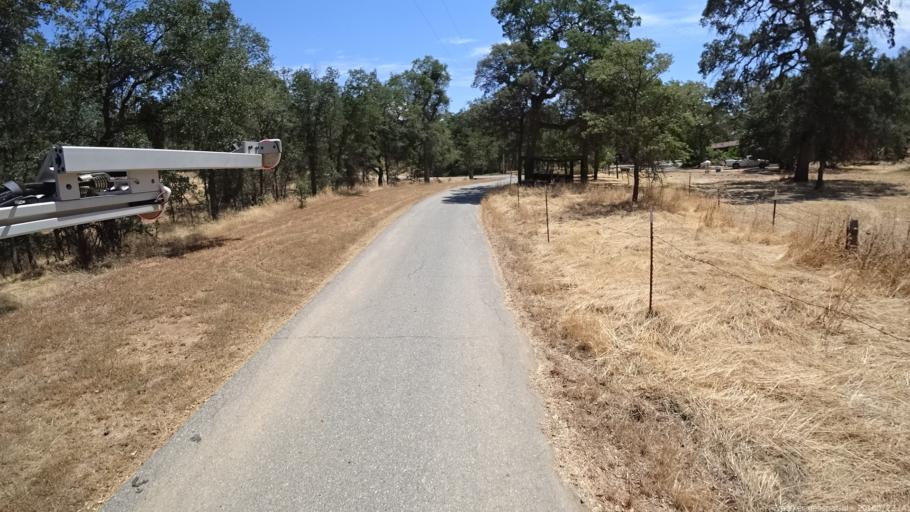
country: US
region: California
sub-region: Madera County
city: Coarsegold
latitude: 37.2532
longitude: -119.7350
